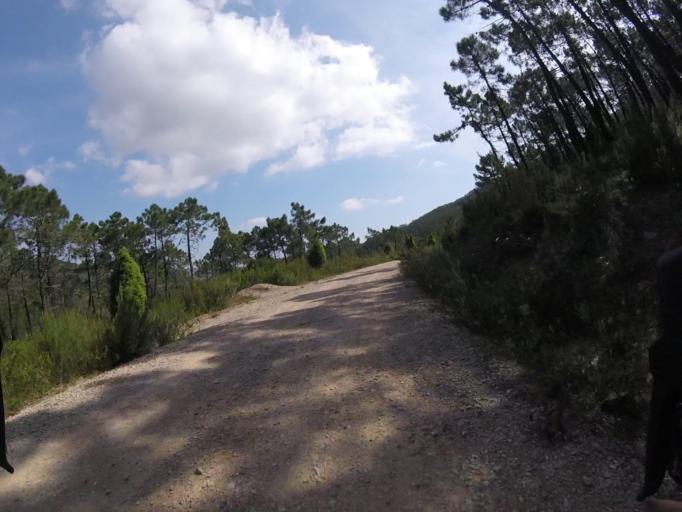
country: ES
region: Valencia
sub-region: Provincia de Castello
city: Cabanes
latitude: 40.1012
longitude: 0.0353
